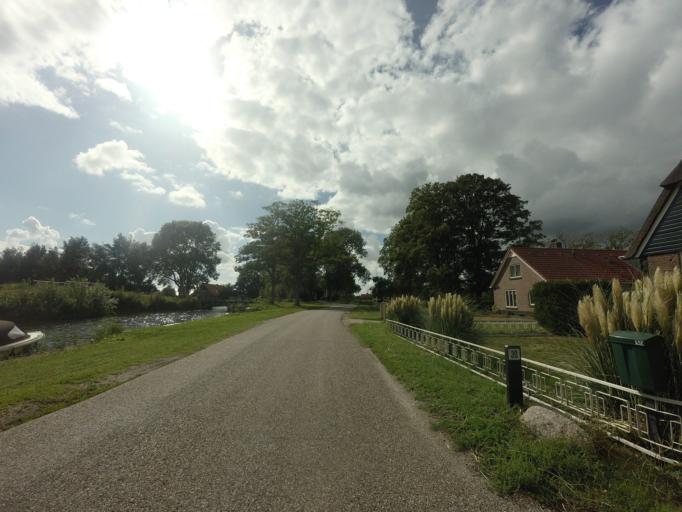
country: NL
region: Overijssel
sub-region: Gemeente Steenwijkerland
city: Giethoorn
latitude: 52.7220
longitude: 6.0647
